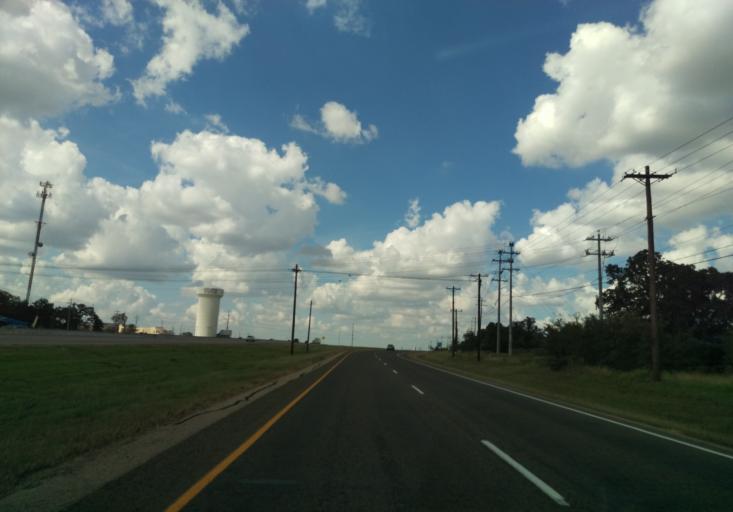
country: US
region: Texas
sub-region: Brazos County
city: College Station
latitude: 30.5559
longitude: -96.2531
